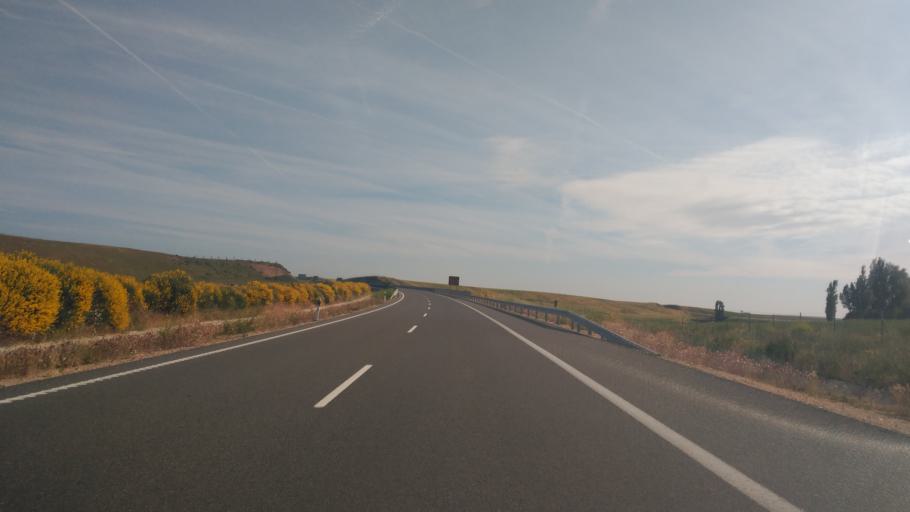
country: ES
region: Castille and Leon
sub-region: Provincia de Salamanca
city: Monterrubio de Armuna
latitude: 41.0374
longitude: -5.6682
